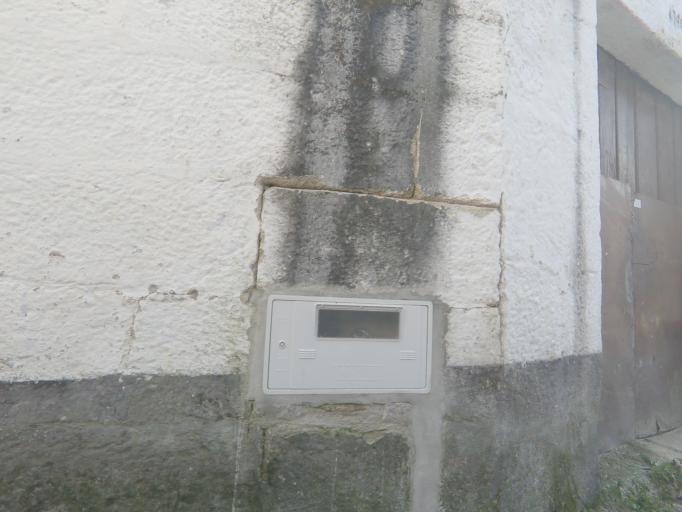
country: PT
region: Vila Real
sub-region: Vila Real
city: Vila Real
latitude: 41.3219
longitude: -7.7818
